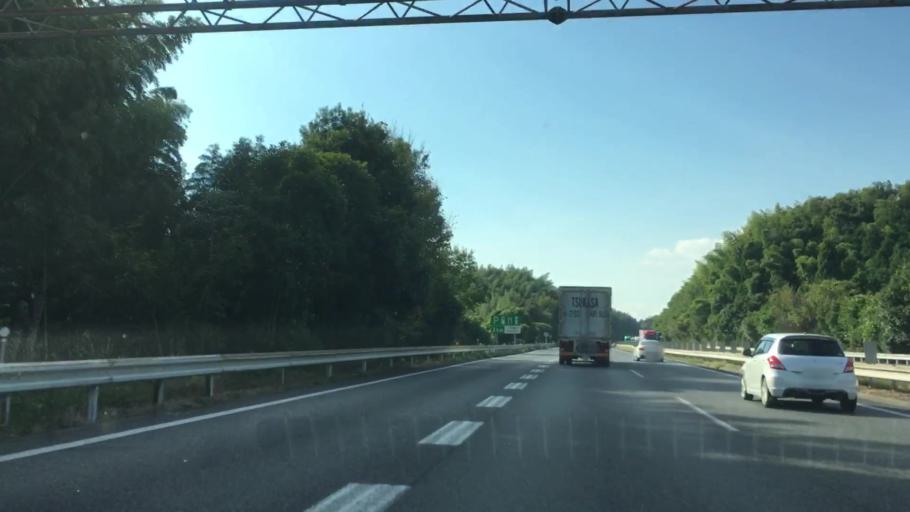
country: JP
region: Yamaguchi
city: Hikari
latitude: 34.0304
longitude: 131.9392
